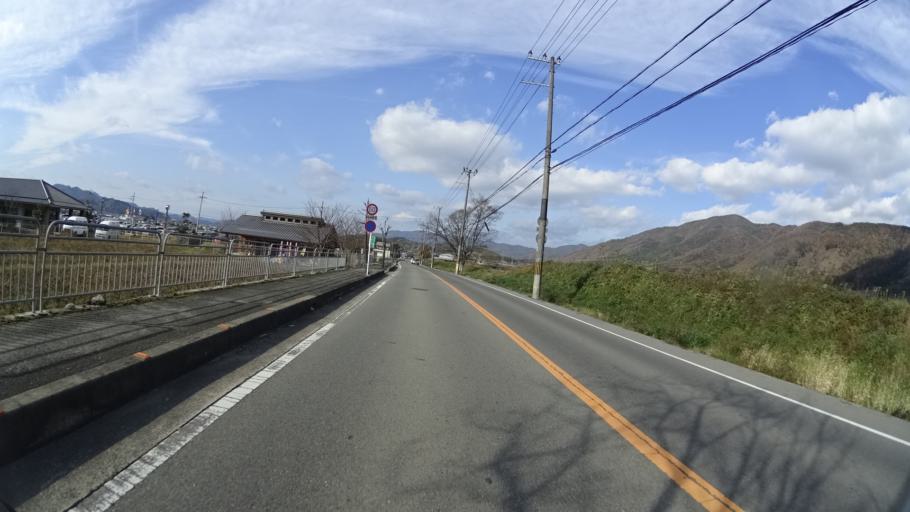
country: JP
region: Kyoto
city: Kameoka
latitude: 35.0488
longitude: 135.5748
